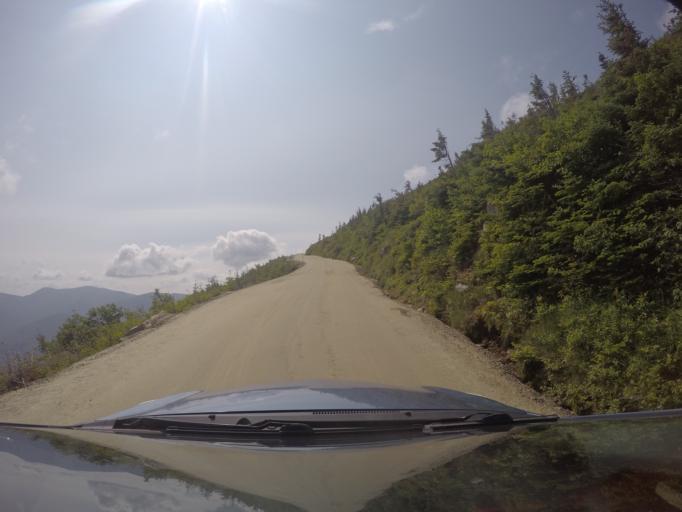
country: US
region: New Hampshire
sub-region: Coos County
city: Gorham
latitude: 44.2859
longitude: -71.2777
